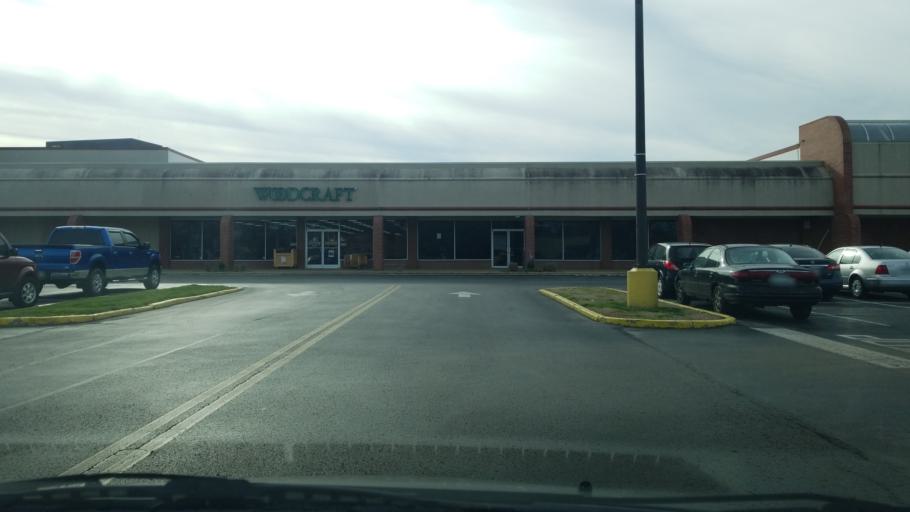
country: US
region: Tennessee
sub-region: Hamilton County
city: East Ridge
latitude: 35.0116
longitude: -85.2117
